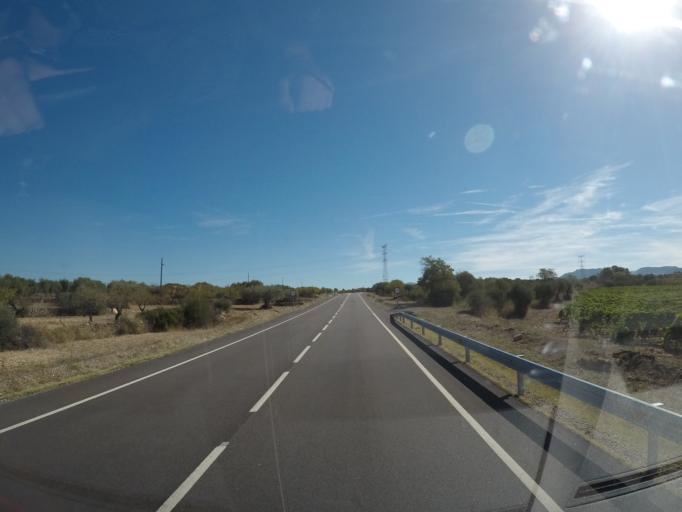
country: ES
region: Catalonia
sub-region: Provincia de Tarragona
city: Garcia
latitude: 41.1080
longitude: 0.6847
